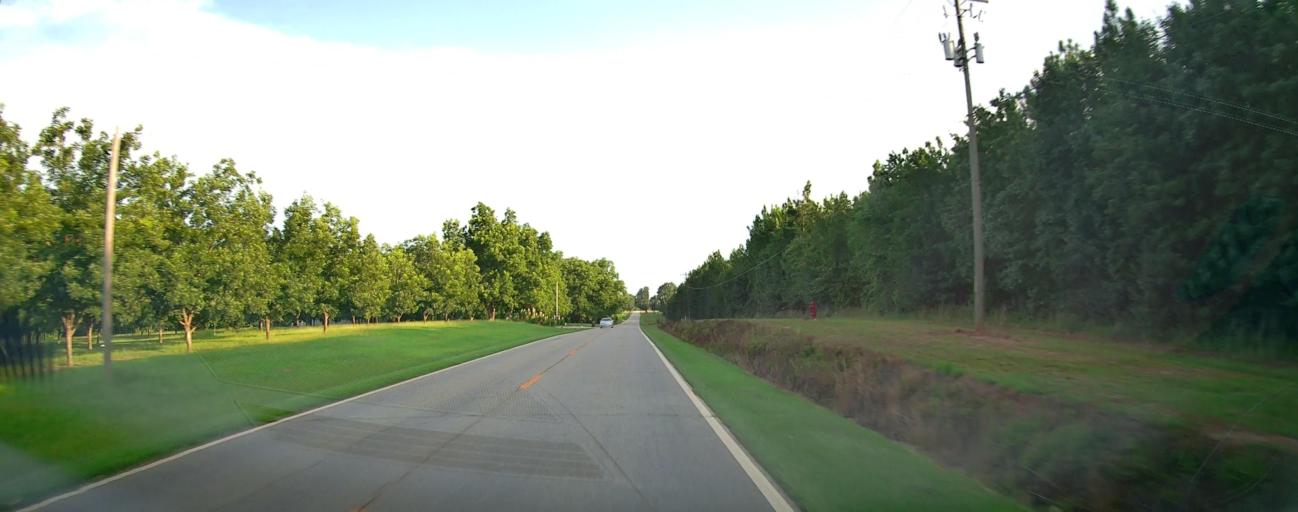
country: US
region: Georgia
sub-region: Peach County
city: Byron
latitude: 32.6683
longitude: -83.8609
